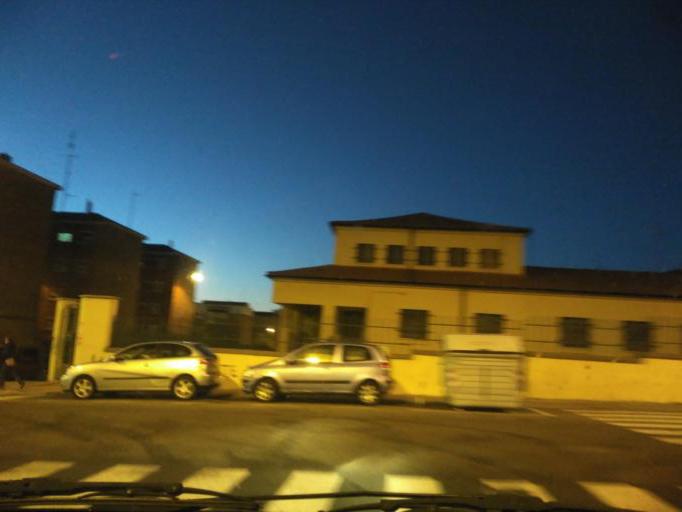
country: ES
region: Castille and Leon
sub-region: Provincia de Salamanca
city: Salamanca
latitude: 40.9703
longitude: -5.6722
